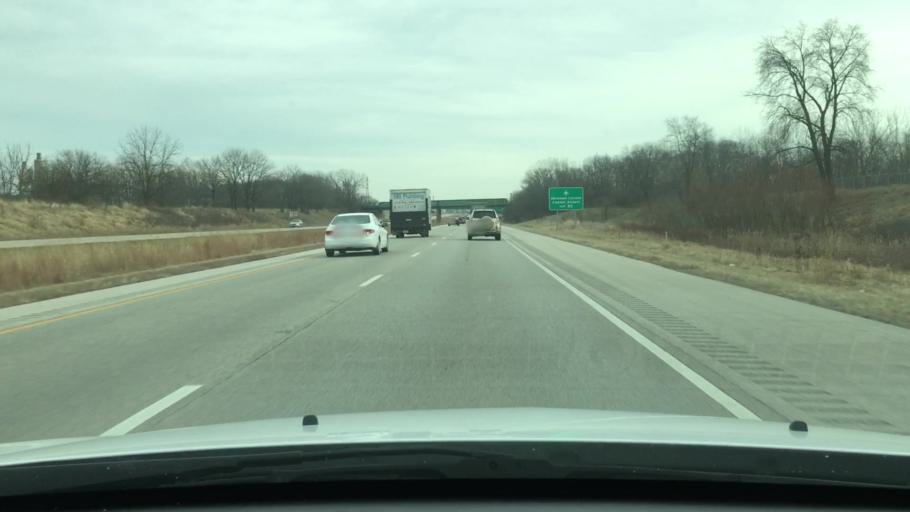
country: US
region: Illinois
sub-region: Sangamon County
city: Jerome
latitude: 39.7459
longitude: -89.7171
